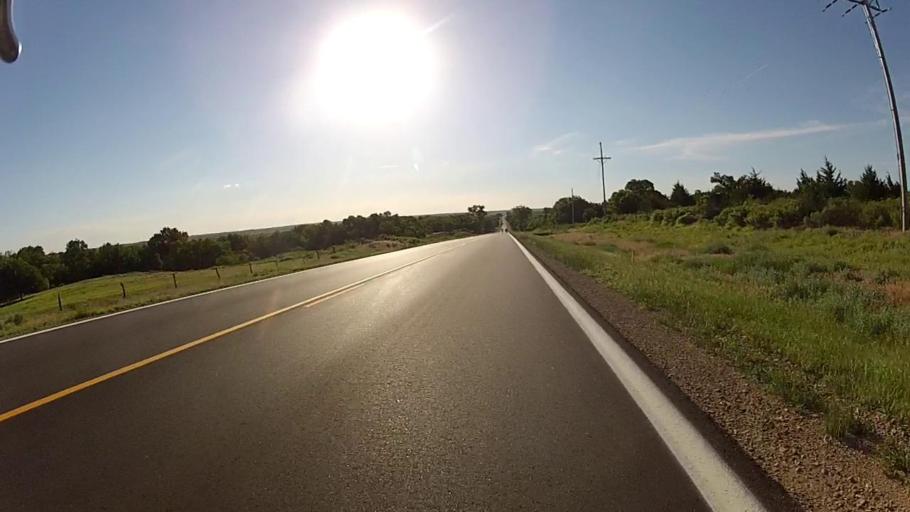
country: US
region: Kansas
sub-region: Comanche County
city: Coldwater
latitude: 37.2820
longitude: -99.0849
